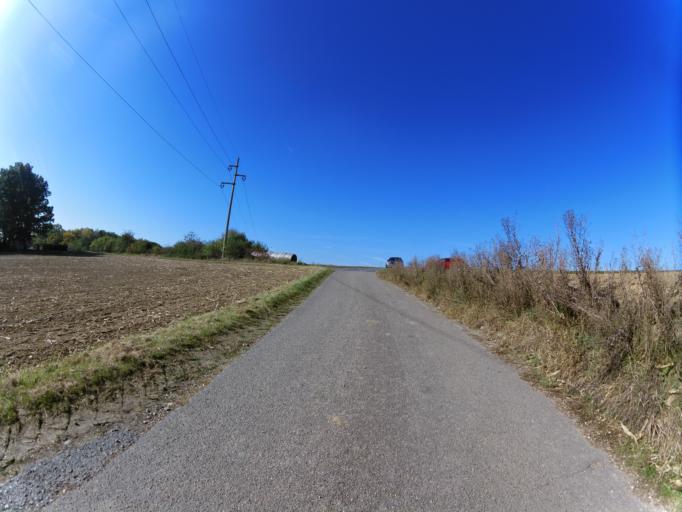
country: DE
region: Bavaria
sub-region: Regierungsbezirk Unterfranken
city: Ochsenfurt
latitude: 49.6779
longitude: 10.0552
